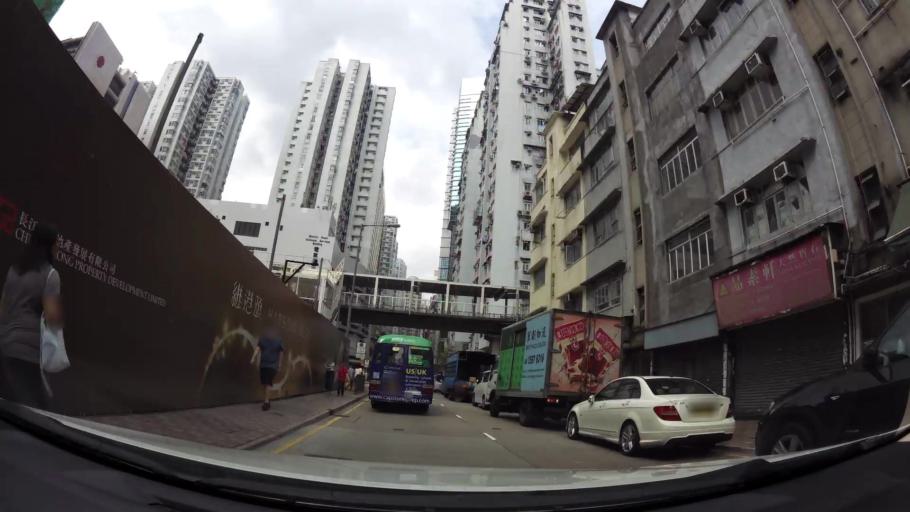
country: HK
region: Wanchai
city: Wan Chai
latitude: 22.2891
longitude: 114.1930
